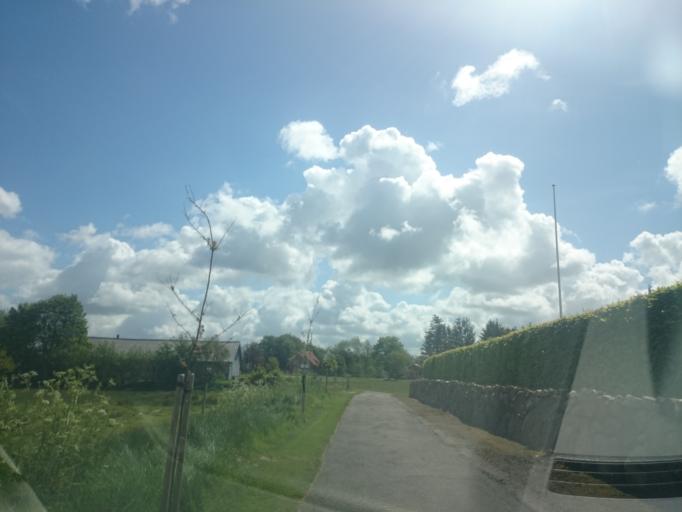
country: DK
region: South Denmark
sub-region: Billund Kommune
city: Grindsted
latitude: 55.6466
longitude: 8.8069
